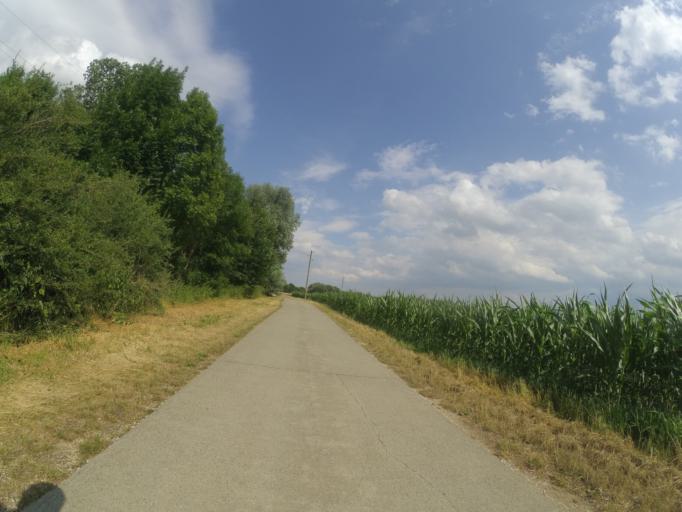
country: DE
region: Baden-Wuerttemberg
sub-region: Tuebingen Region
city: Opfingen
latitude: 48.2796
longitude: 9.8129
